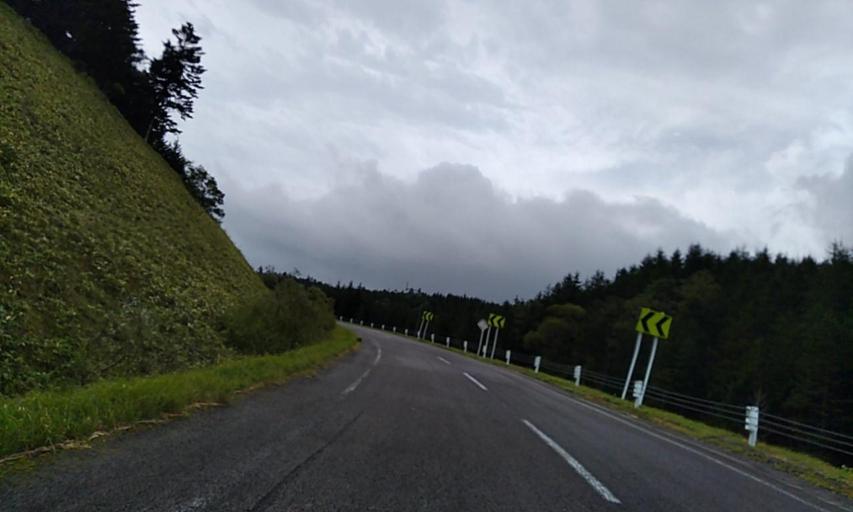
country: JP
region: Hokkaido
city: Abashiri
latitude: 43.6196
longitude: 144.5807
